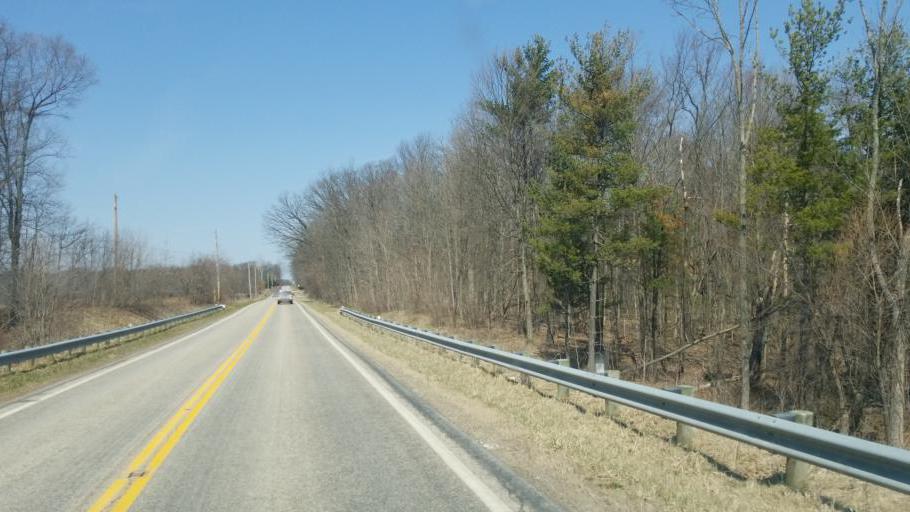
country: US
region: Ohio
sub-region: Ashland County
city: Loudonville
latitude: 40.7434
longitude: -82.2067
